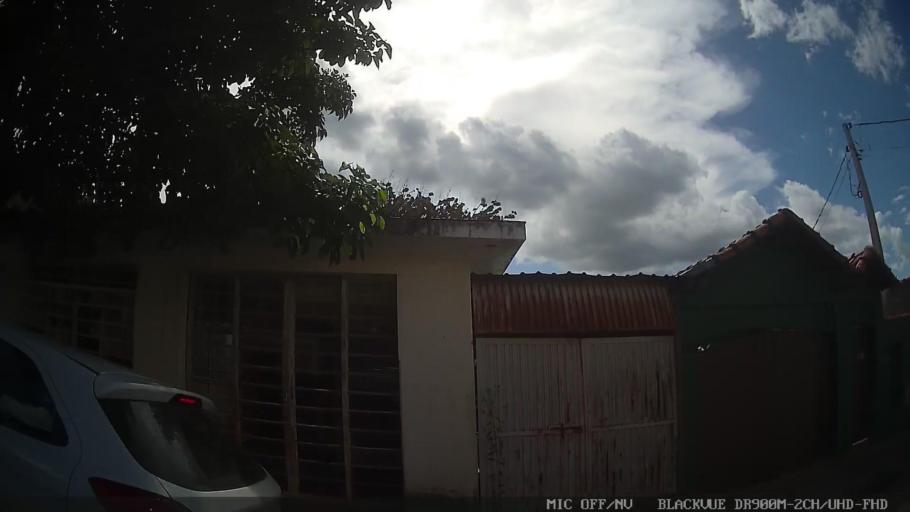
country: BR
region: Sao Paulo
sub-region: Conchas
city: Conchas
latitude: -23.0160
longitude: -48.0117
